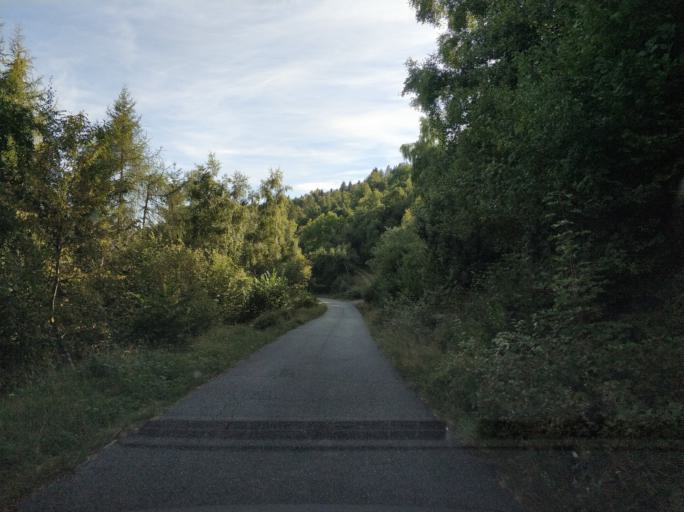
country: IT
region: Piedmont
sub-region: Provincia di Torino
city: Monastero di Lanzo
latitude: 45.3174
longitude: 7.4199
